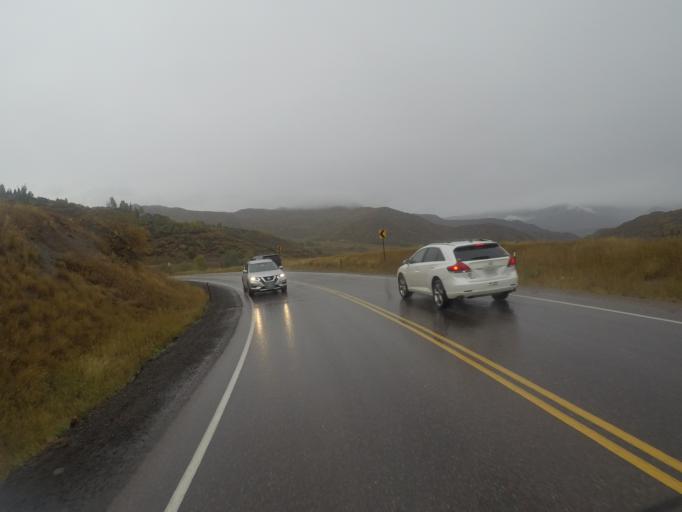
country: US
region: Colorado
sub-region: Pitkin County
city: Snowmass Village
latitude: 39.2194
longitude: -106.9316
